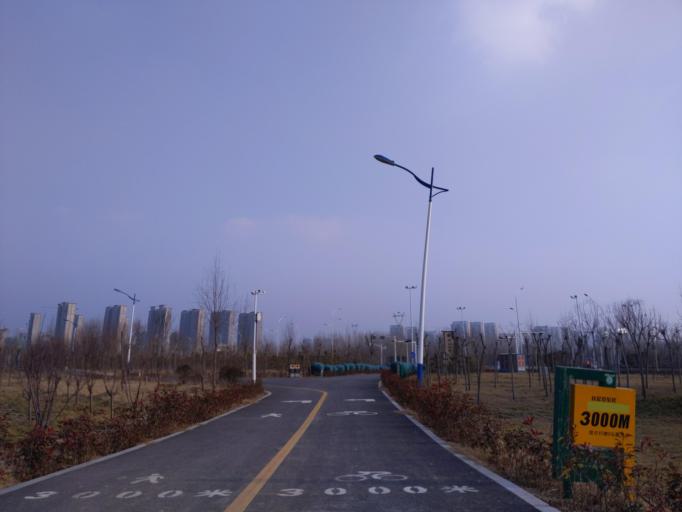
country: CN
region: Henan Sheng
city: Puyang
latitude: 35.8197
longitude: 114.9995
